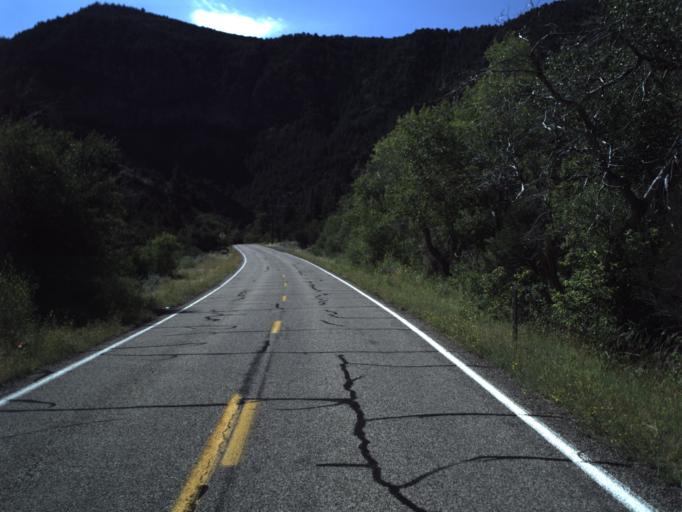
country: US
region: Utah
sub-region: Beaver County
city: Beaver
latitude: 38.2580
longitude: -112.5433
